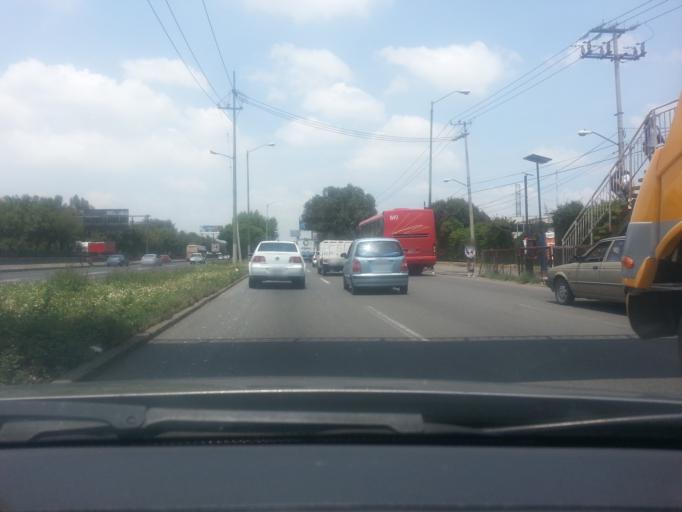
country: MX
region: Mexico
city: Cuautitlan Izcalli
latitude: 19.6516
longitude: -99.1967
